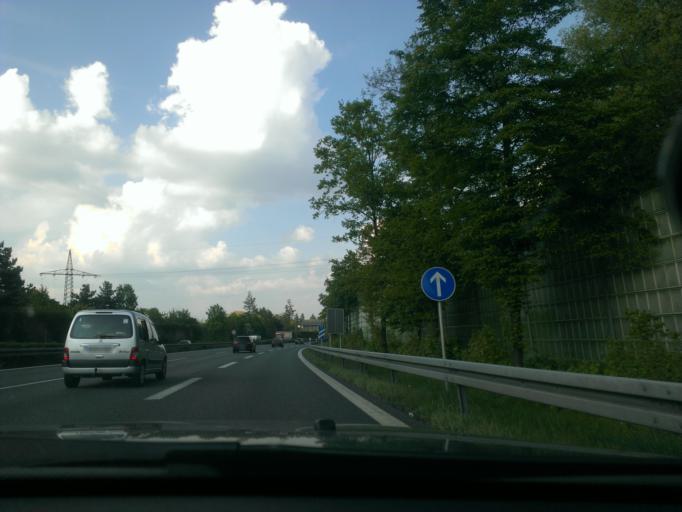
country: DE
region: Bavaria
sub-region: Regierungsbezirk Mittelfranken
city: Erlangen
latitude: 49.5858
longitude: 10.9894
